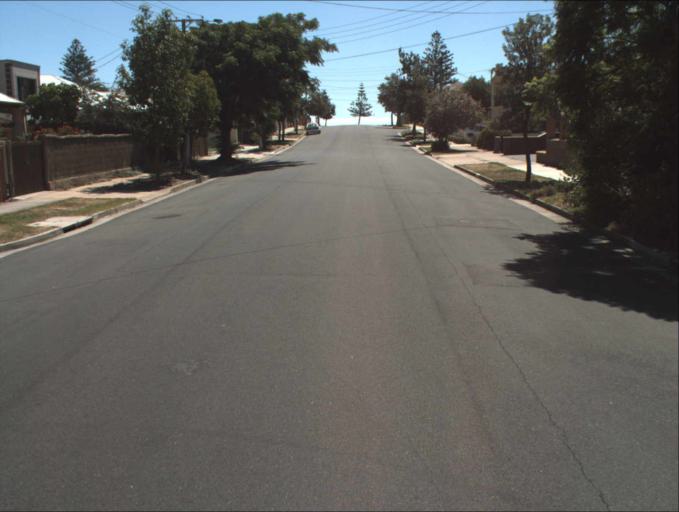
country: AU
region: South Australia
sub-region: Port Adelaide Enfield
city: Birkenhead
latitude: -34.8186
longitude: 138.4924
